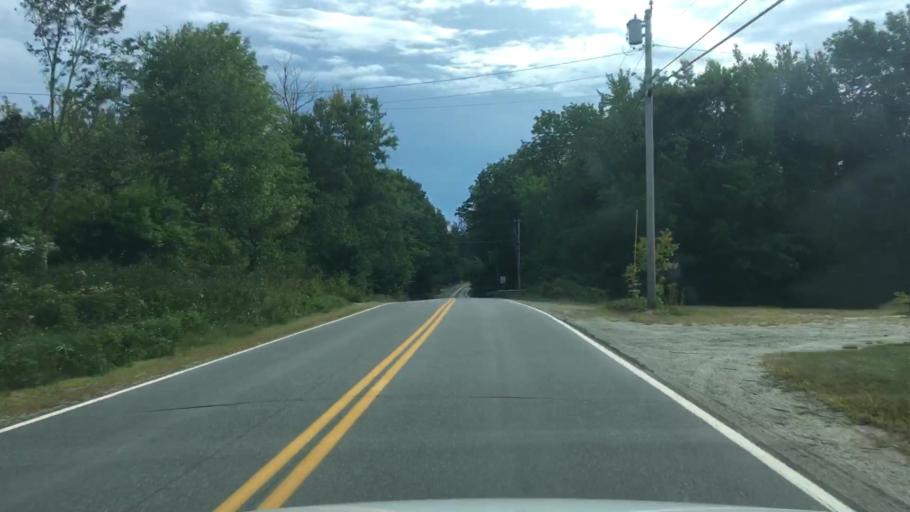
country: US
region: Maine
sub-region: Hancock County
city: Trenton
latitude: 44.4640
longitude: -68.4242
